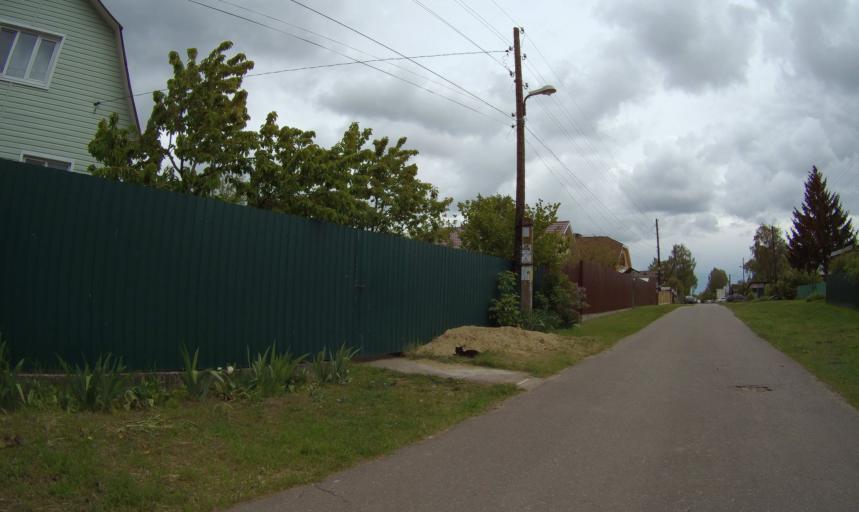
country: RU
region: Moskovskaya
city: Raduzhnyy
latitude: 55.1181
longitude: 38.7619
